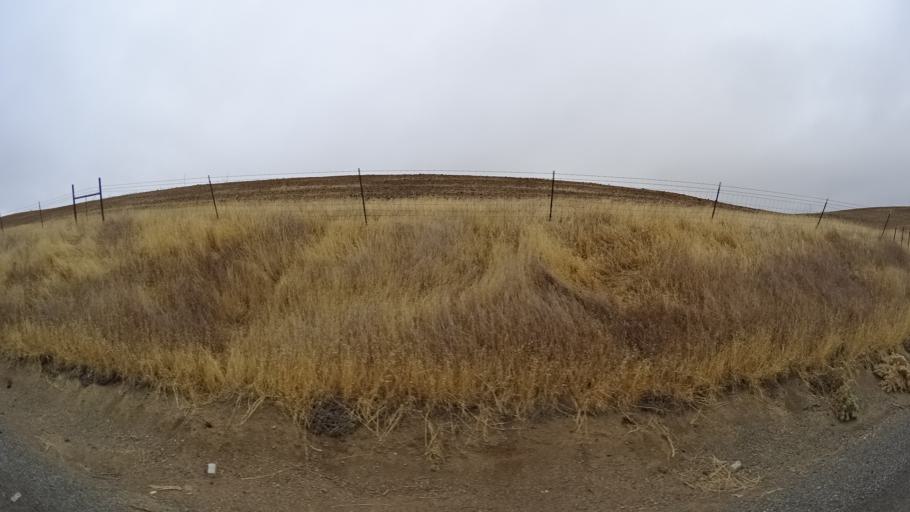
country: US
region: California
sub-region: Yolo County
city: Dunnigan
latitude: 38.8835
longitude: -122.0108
